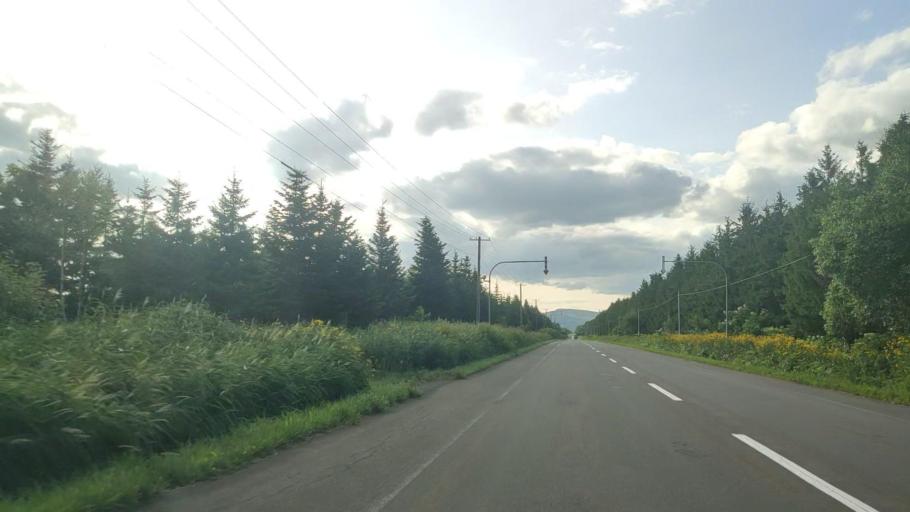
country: JP
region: Hokkaido
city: Makubetsu
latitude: 44.8862
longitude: 142.0096
